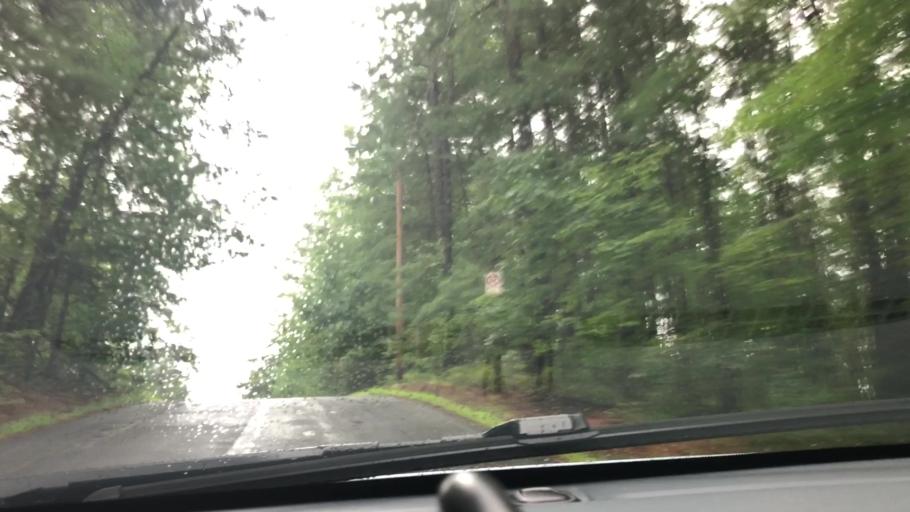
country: US
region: New Hampshire
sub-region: Hillsborough County
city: Pinardville
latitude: 42.9994
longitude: -71.4974
